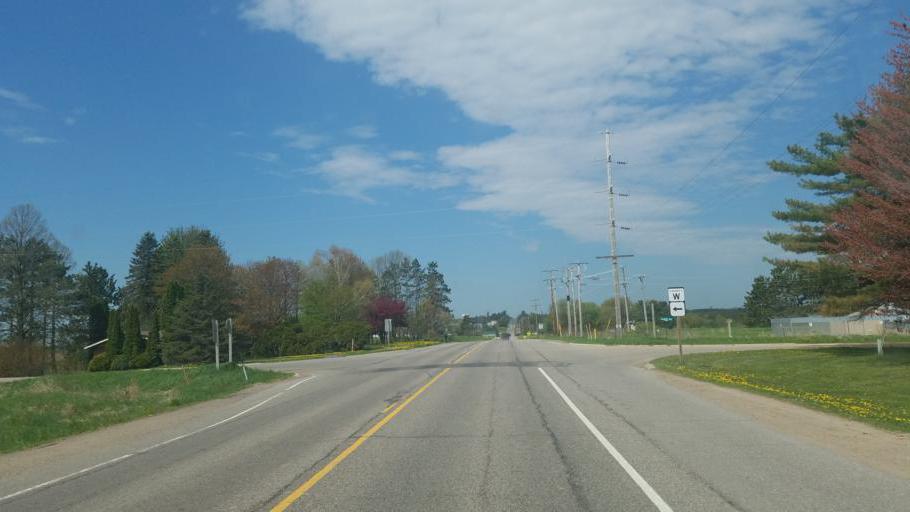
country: US
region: Wisconsin
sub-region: Clark County
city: Loyal
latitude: 44.5825
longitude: -90.3952
